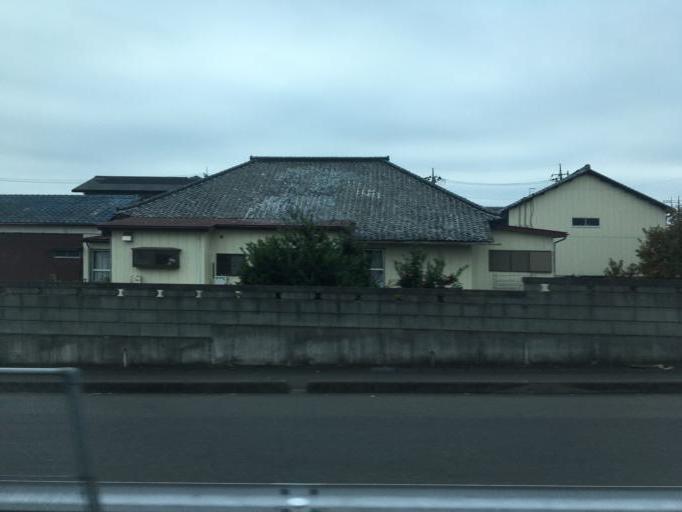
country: JP
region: Tochigi
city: Oyama
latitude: 36.3037
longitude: 139.8318
